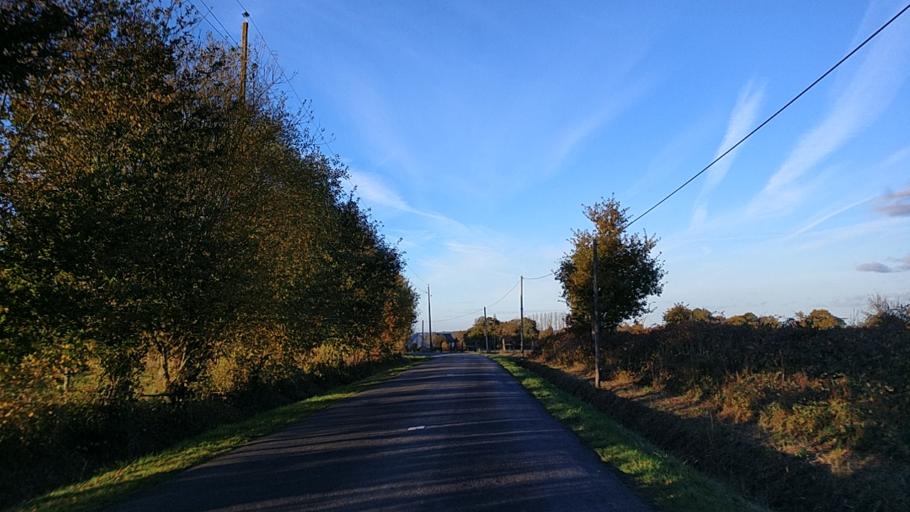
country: FR
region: Brittany
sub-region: Departement d'Ille-et-Vilaine
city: Saint-Sulpice-la-Foret
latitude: 48.2030
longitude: -1.5767
